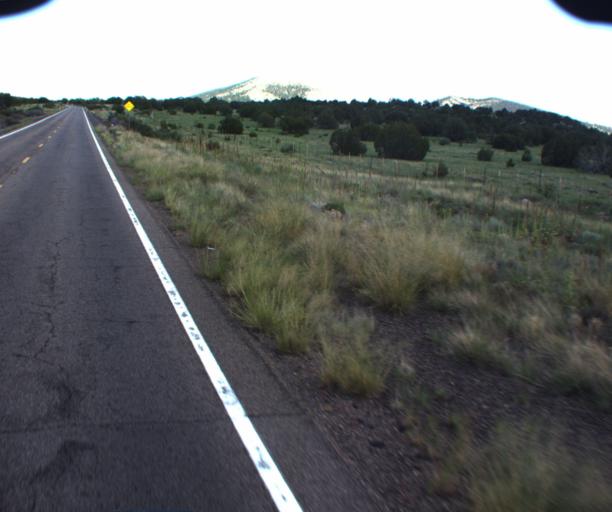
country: US
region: Arizona
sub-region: Apache County
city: Saint Johns
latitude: 34.2679
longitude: -109.6221
